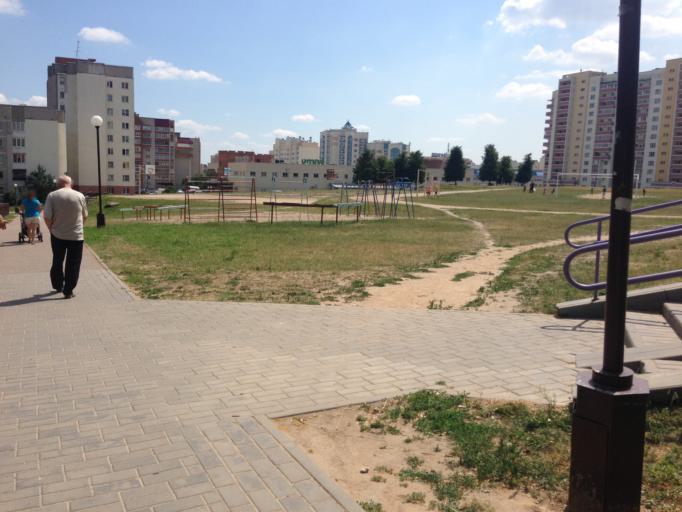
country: BY
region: Grodnenskaya
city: Hrodna
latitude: 53.7122
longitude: 23.8460
